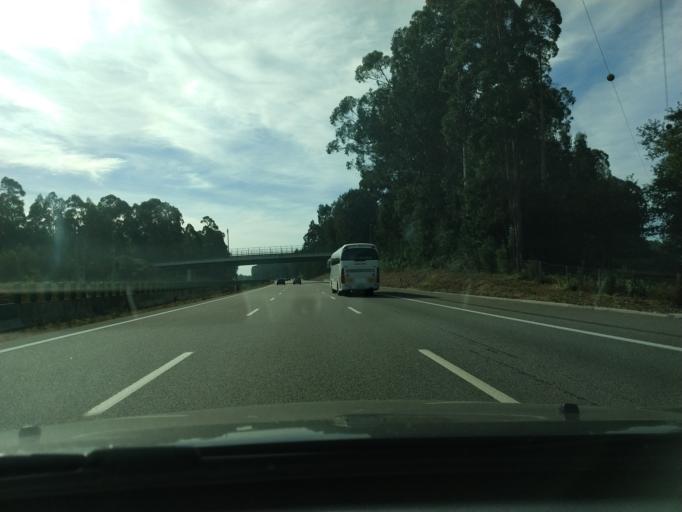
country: PT
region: Aveiro
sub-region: Estarreja
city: Avanca
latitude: 40.8280
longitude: -8.5542
